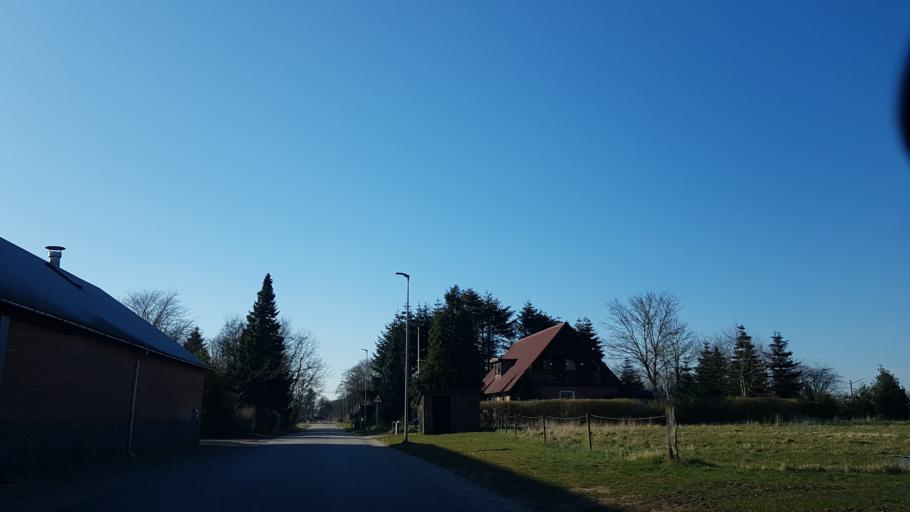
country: DK
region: South Denmark
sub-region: Vejen Kommune
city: Vejen
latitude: 55.4375
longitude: 9.1862
